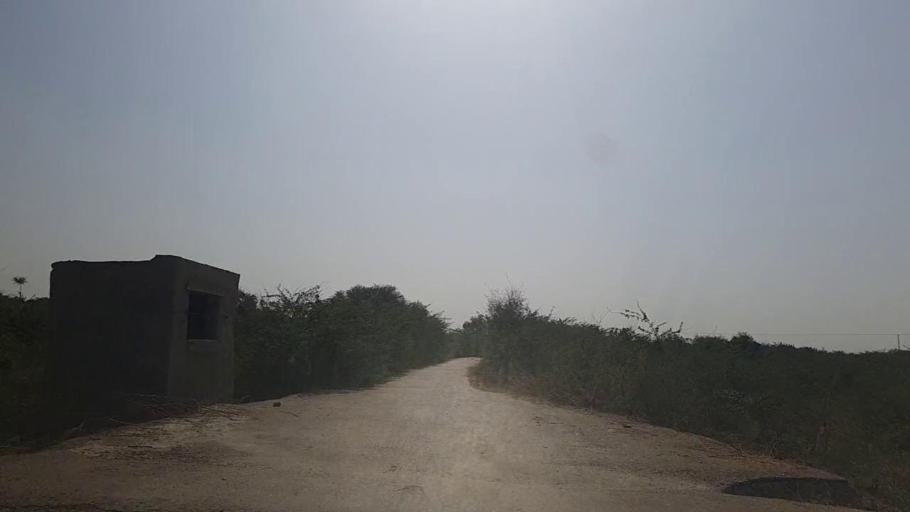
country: PK
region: Sindh
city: Naukot
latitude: 24.5692
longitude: 69.2914
